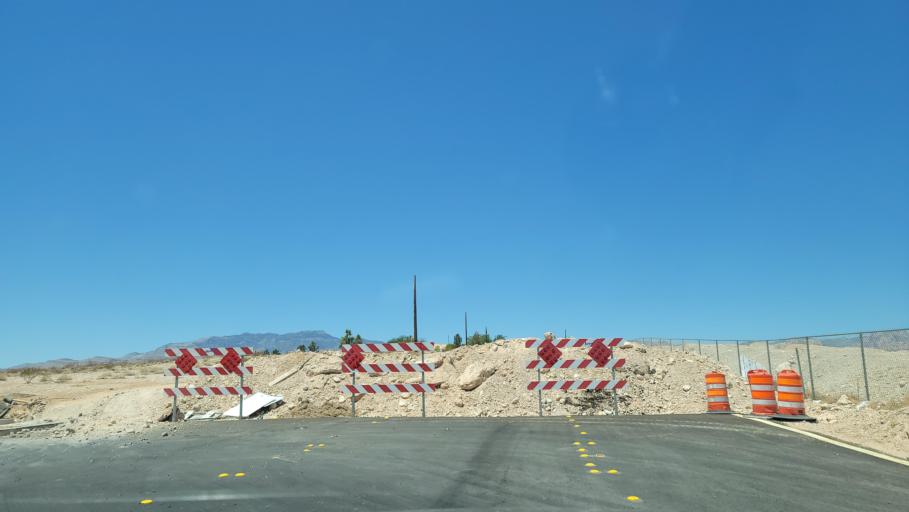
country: US
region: Nevada
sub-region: Clark County
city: Enterprise
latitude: 36.0263
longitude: -115.3033
